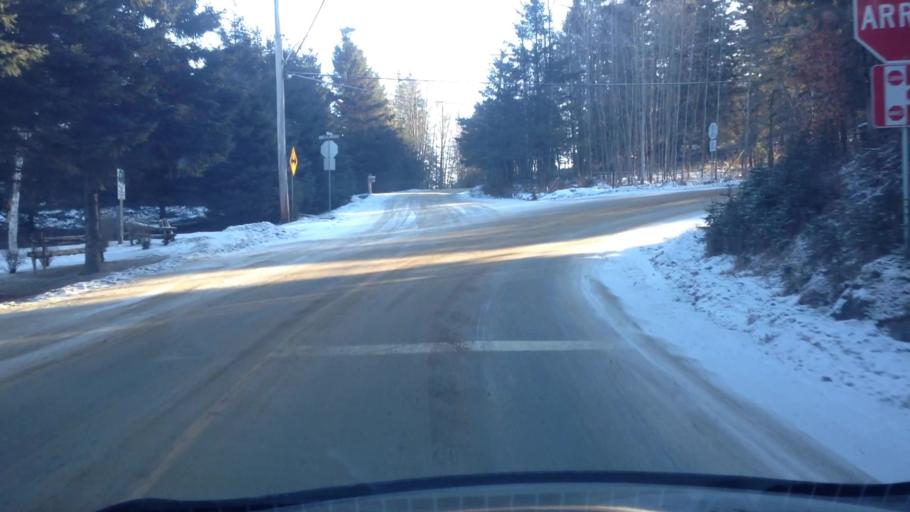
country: CA
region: Quebec
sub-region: Laurentides
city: Mont-Tremblant
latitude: 45.9402
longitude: -74.5454
